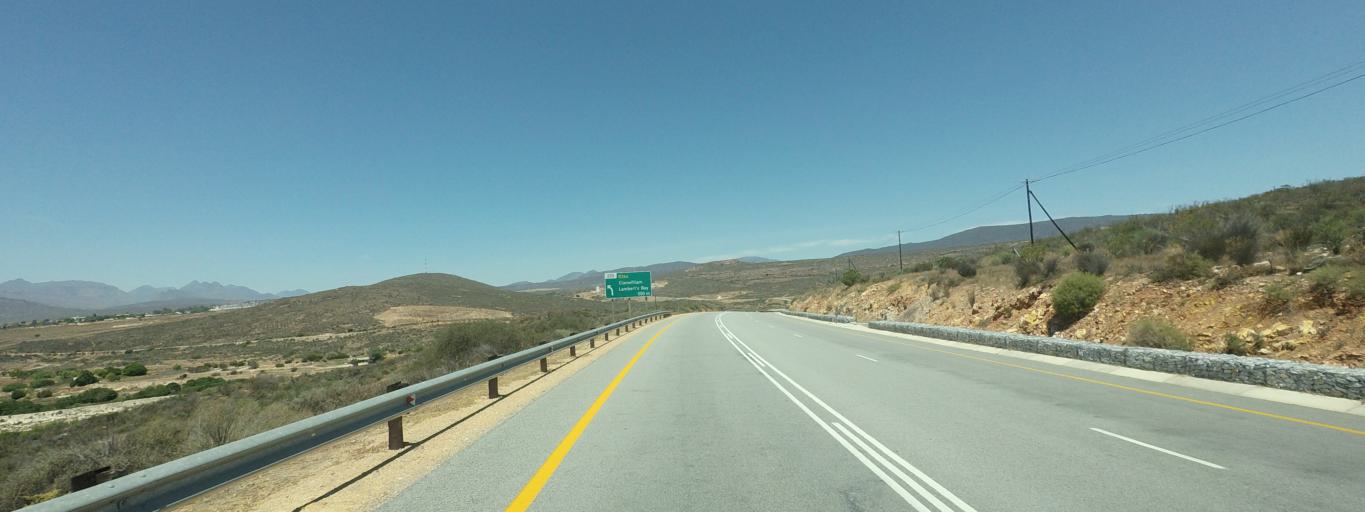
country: ZA
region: Western Cape
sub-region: West Coast District Municipality
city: Clanwilliam
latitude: -32.1650
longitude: 18.8720
